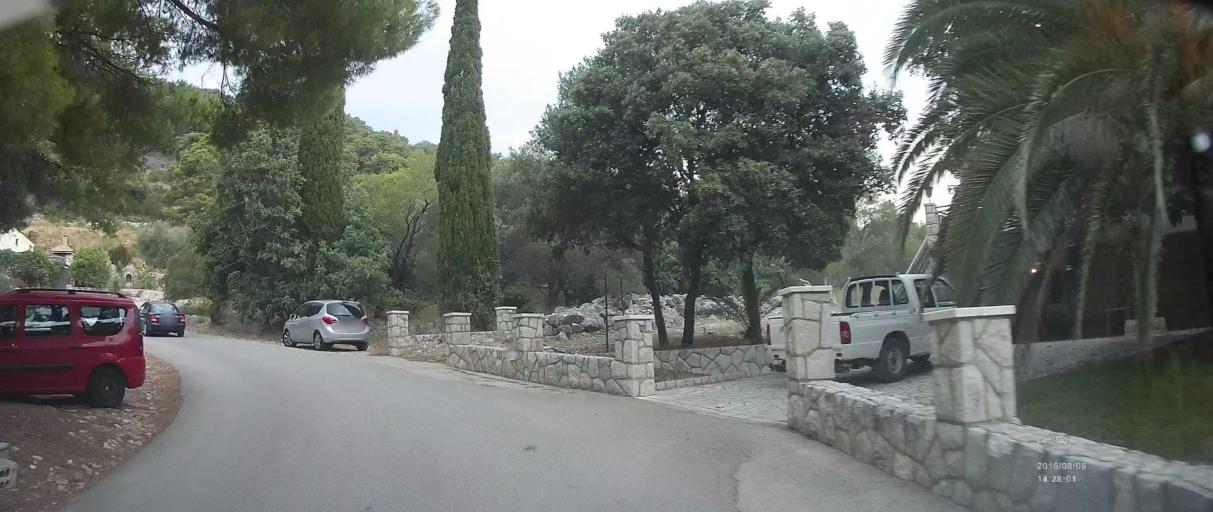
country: HR
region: Dubrovacko-Neretvanska
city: Ston
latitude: 42.7018
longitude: 17.7368
